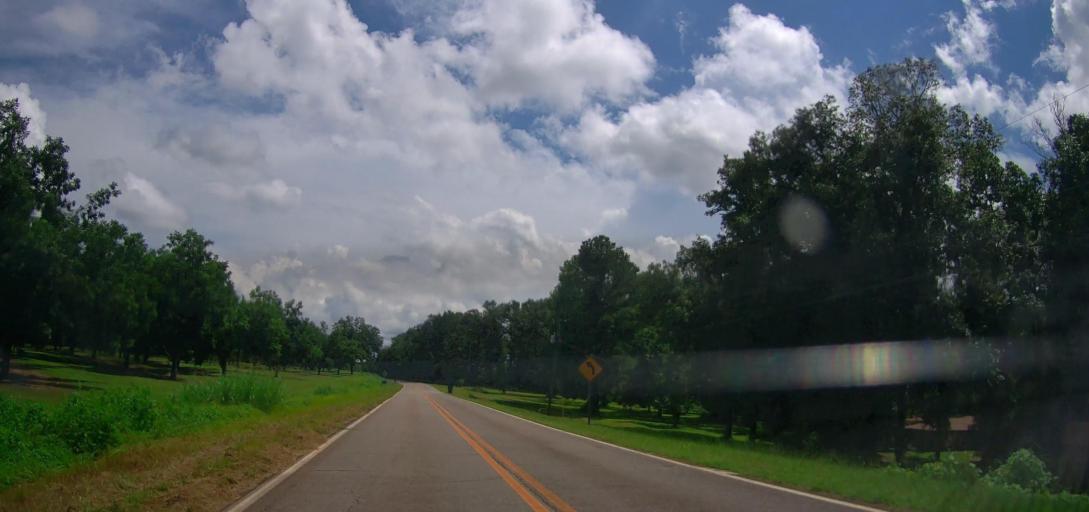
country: US
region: Georgia
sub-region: Peach County
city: Fort Valley
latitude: 32.5234
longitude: -83.8015
